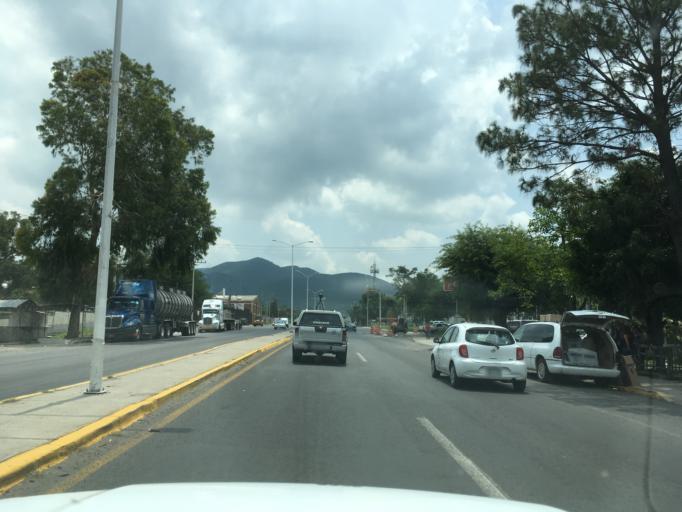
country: MX
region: Jalisco
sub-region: Tlajomulco de Zuniga
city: Santa Cruz de las Flores
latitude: 20.4888
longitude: -103.4951
